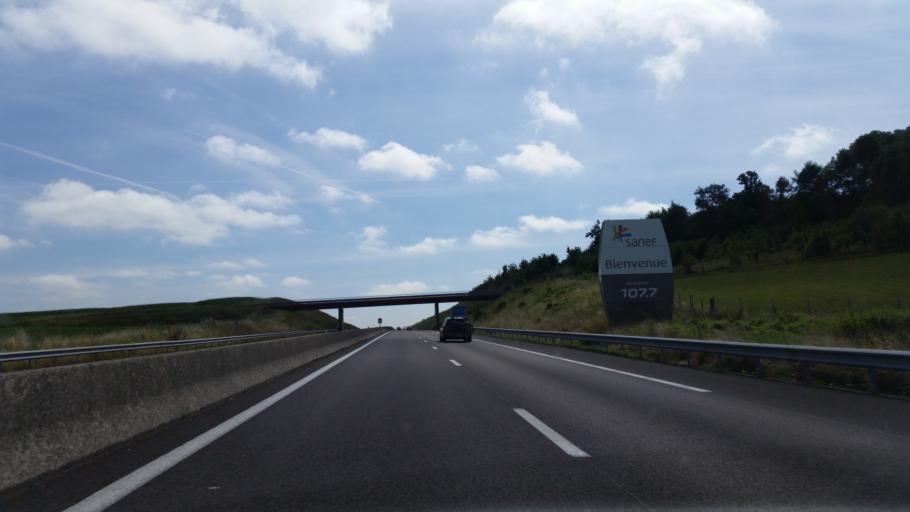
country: FR
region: Haute-Normandie
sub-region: Departement de la Seine-Maritime
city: Neufchatel-en-Bray
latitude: 49.7508
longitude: 1.5088
